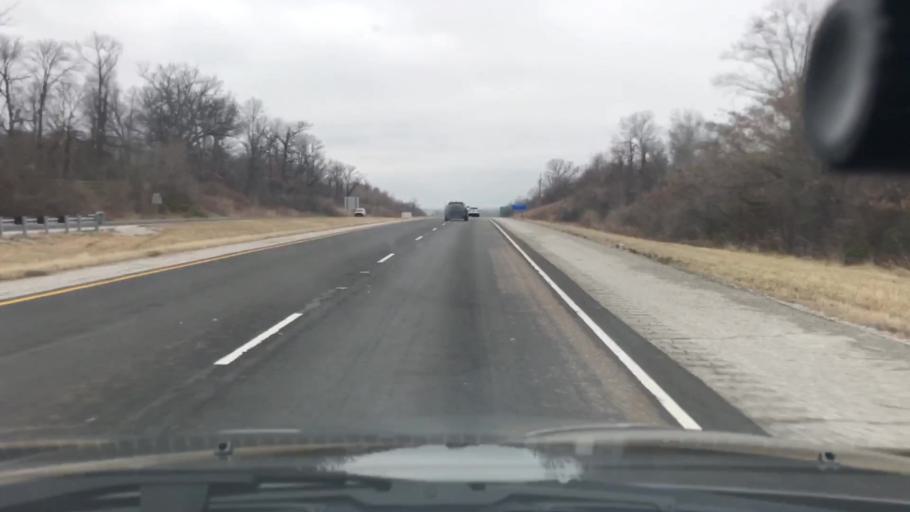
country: US
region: Illinois
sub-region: Madison County
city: Roxana
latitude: 38.8626
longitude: -90.0536
